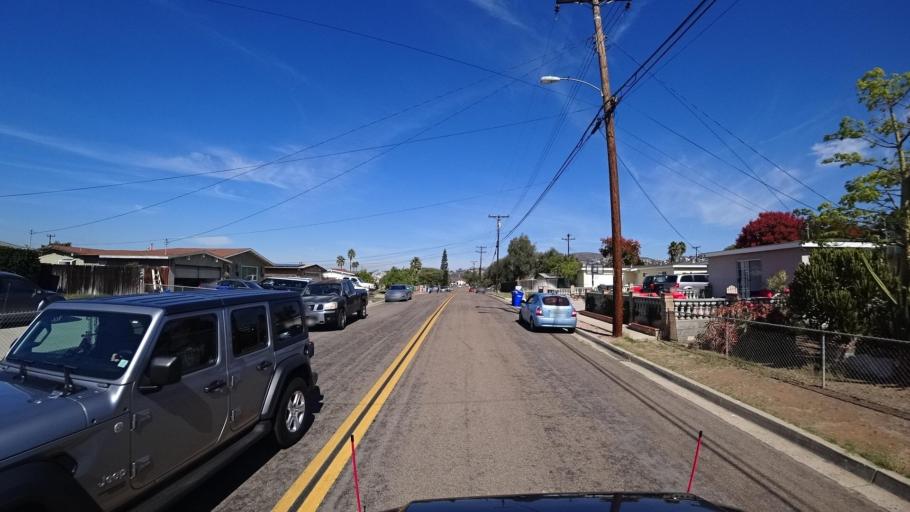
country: US
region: California
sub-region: San Diego County
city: La Presa
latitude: 32.7015
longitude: -117.0042
